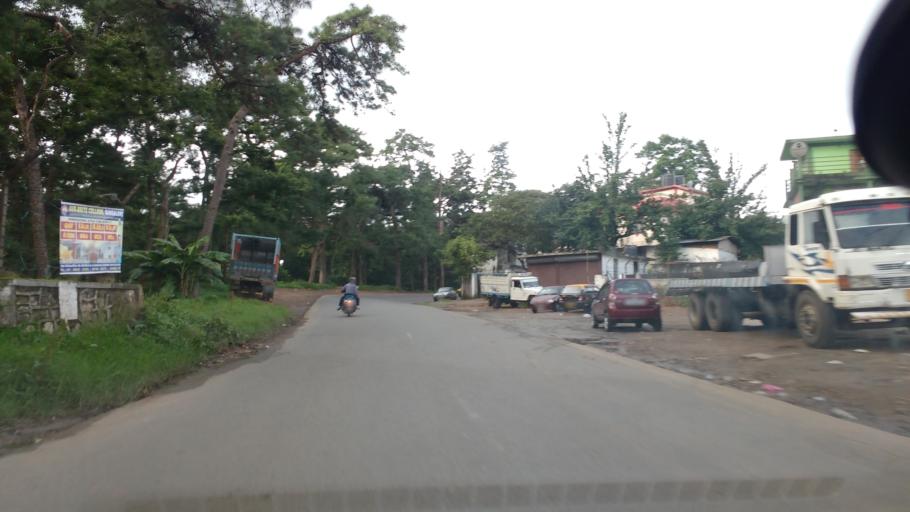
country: IN
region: Meghalaya
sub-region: East Khasi Hills
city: Shillong
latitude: 25.5658
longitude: 91.8553
